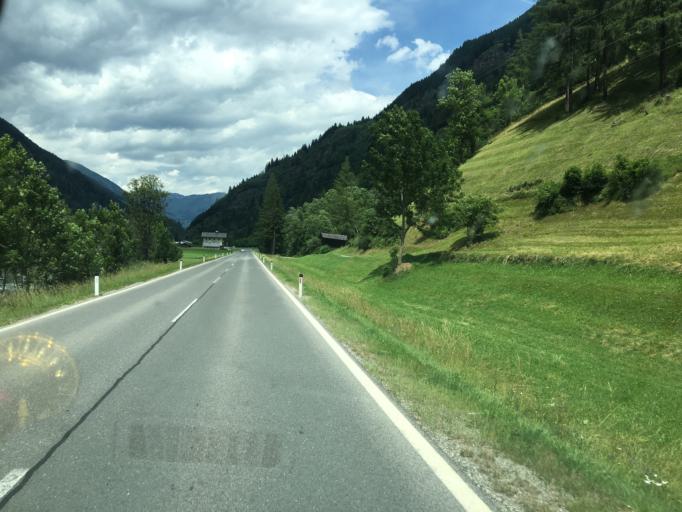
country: AT
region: Carinthia
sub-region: Politischer Bezirk Spittal an der Drau
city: Mortschach
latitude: 46.9293
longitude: 12.9061
